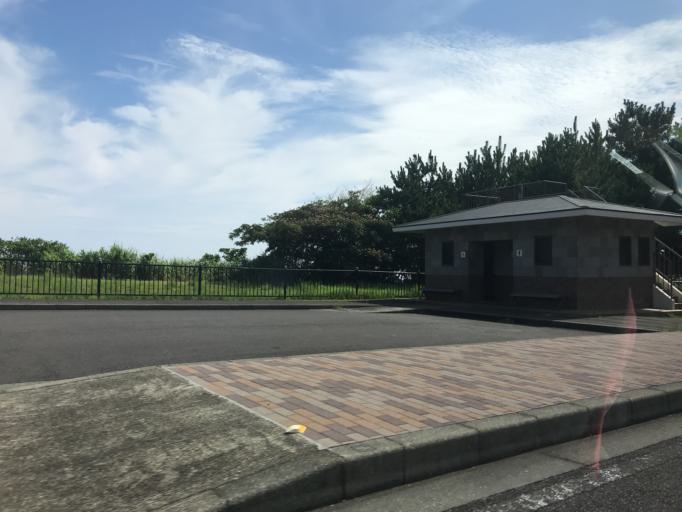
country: JP
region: Shizuoka
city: Ito
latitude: 34.7868
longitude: 139.4013
